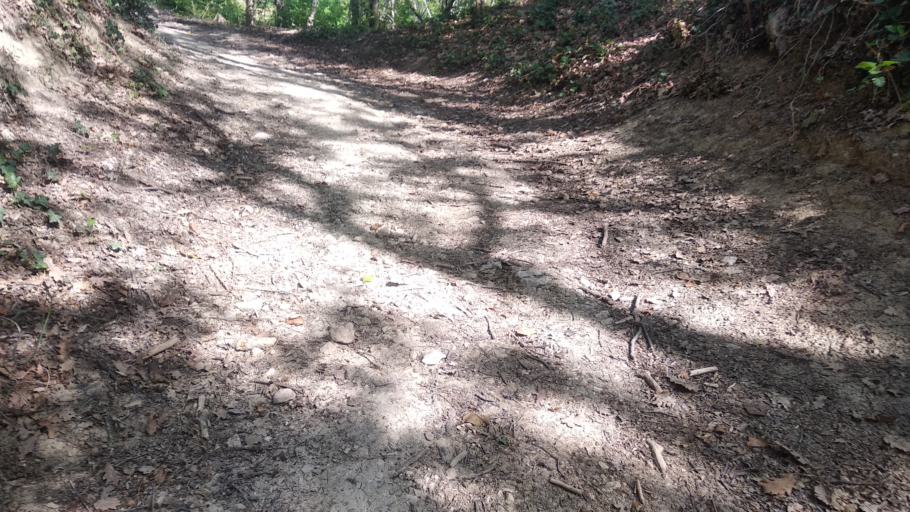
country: IT
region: Emilia-Romagna
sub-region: Provincia di Ravenna
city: Fognano
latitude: 44.2252
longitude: 11.7241
